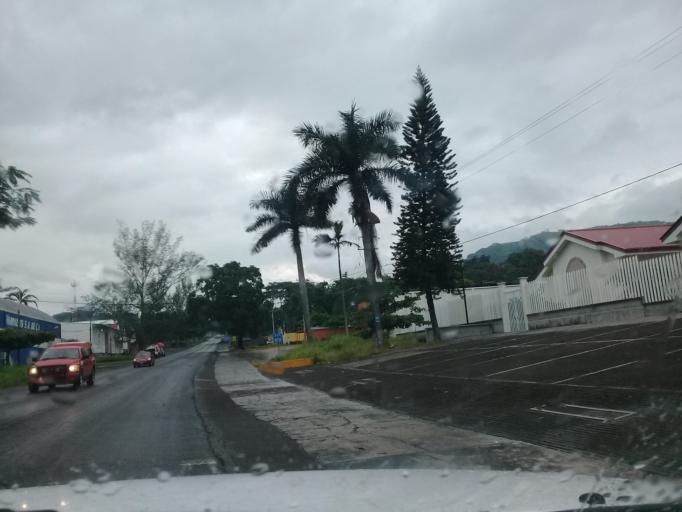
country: MX
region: Veracruz
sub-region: San Andres Tuxtla
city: Matacapan
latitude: 18.4349
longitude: -95.1905
